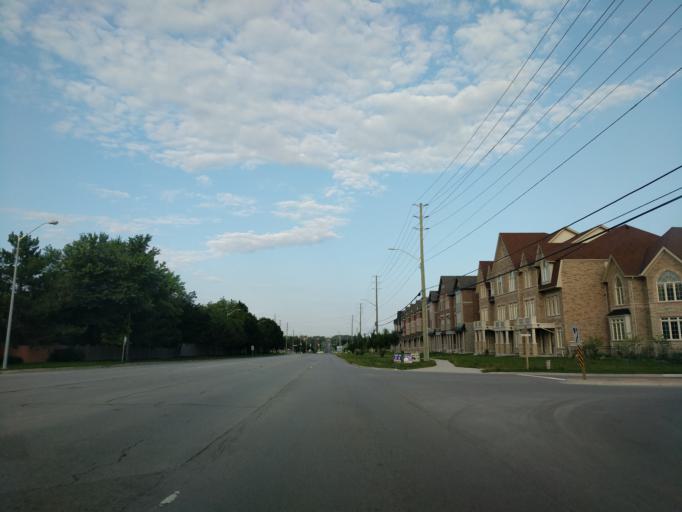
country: CA
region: Ontario
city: Markham
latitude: 43.8805
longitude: -79.3103
